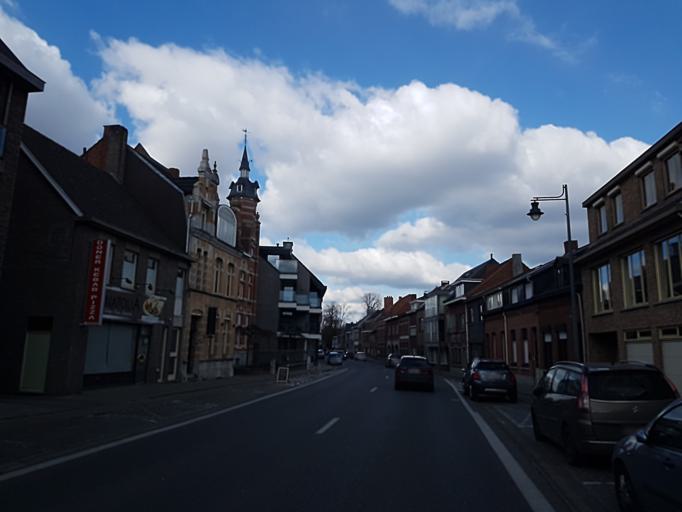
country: BE
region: Flanders
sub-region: Provincie Antwerpen
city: Hoogstraten
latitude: 51.4051
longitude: 4.7630
